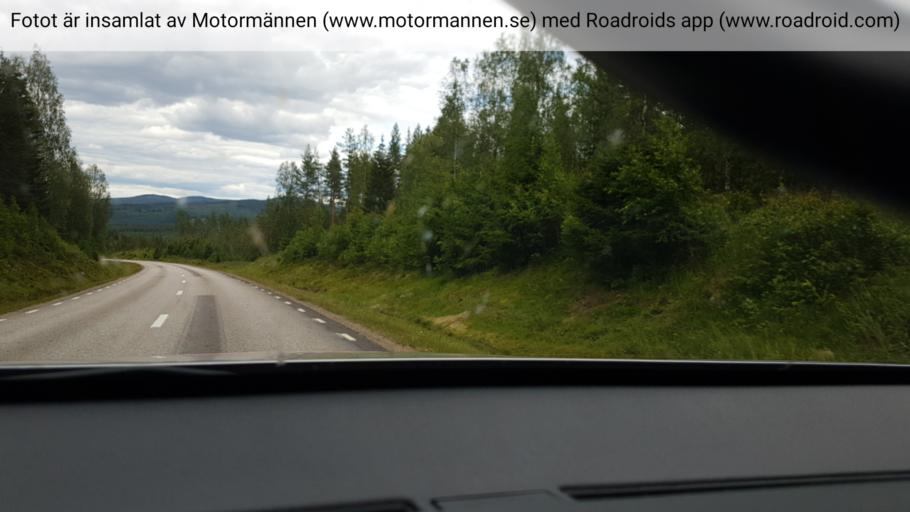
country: NO
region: Hedmark
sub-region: Trysil
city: Innbygda
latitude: 61.0189
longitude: 12.5211
